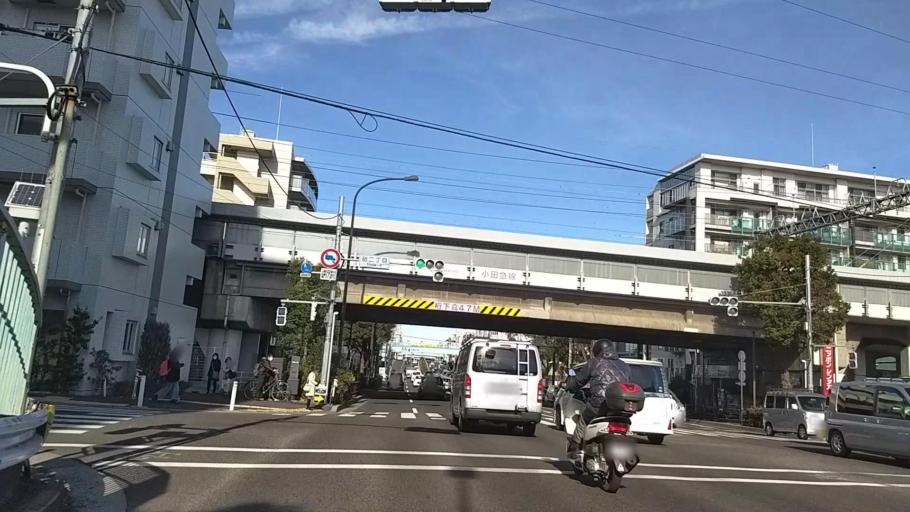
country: JP
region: Tokyo
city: Mitaka-shi
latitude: 35.6452
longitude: 139.6180
